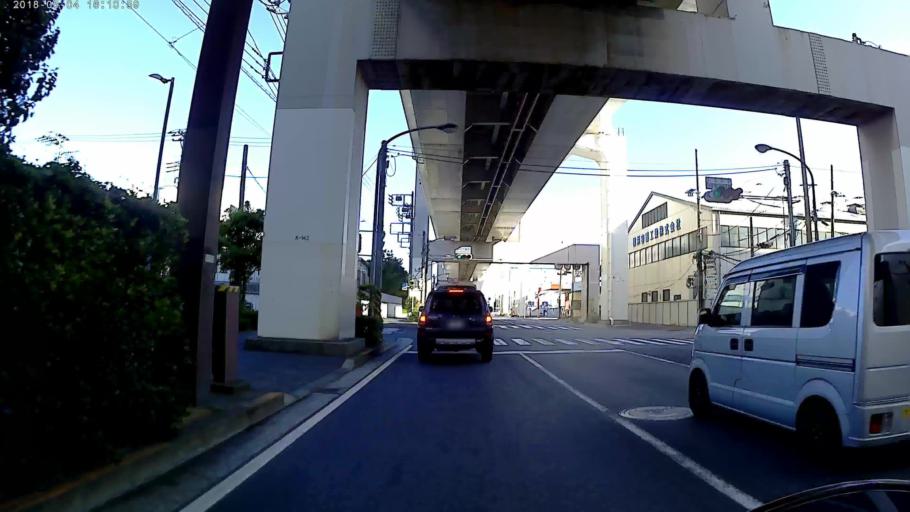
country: JP
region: Kanagawa
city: Yokohama
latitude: 35.4887
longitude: 139.6728
